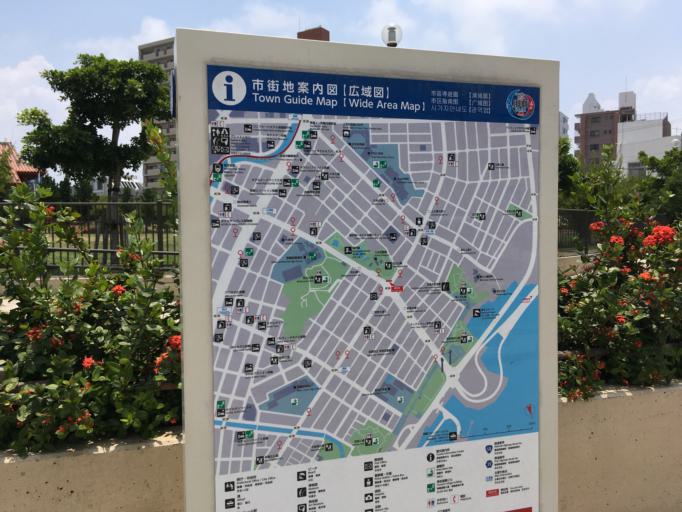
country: JP
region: Okinawa
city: Naha-shi
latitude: 26.2191
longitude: 127.6749
